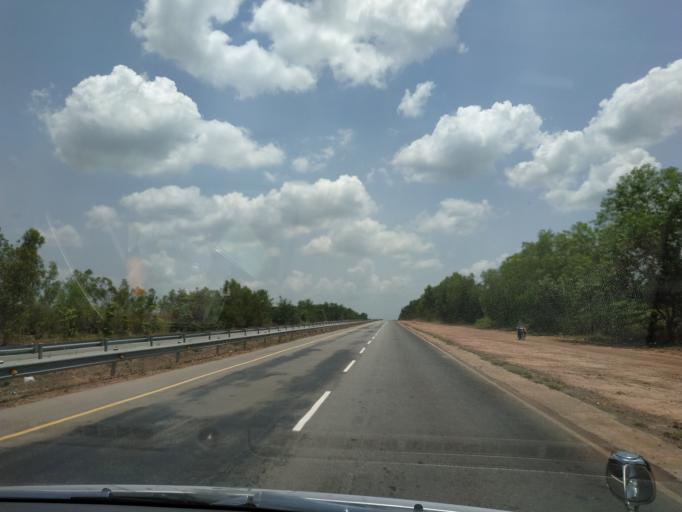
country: MM
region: Bago
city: Thanatpin
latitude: 17.2758
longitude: 96.2297
